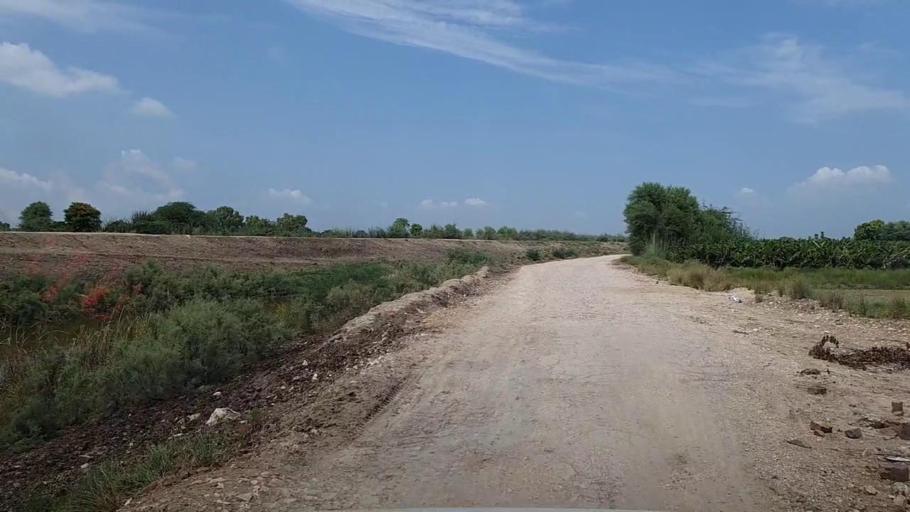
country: PK
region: Sindh
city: Bhiria
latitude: 26.9063
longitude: 68.2017
